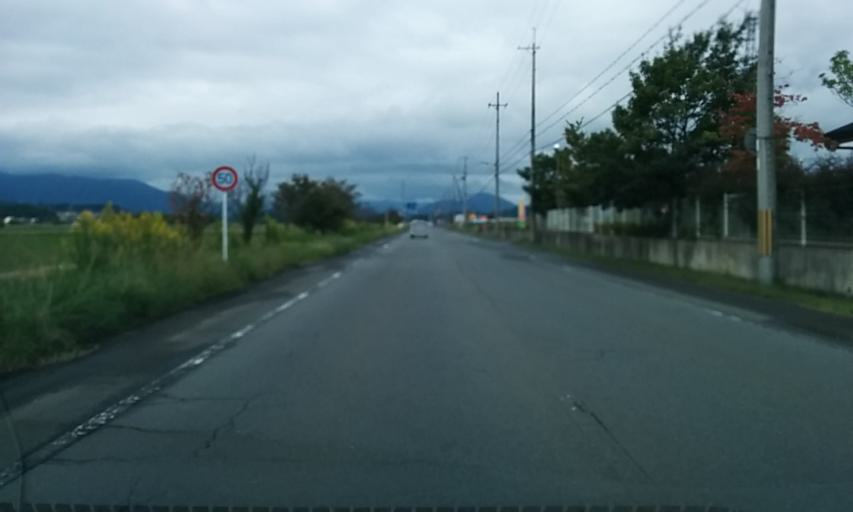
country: JP
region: Kyoto
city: Fukuchiyama
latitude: 35.3055
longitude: 135.1736
